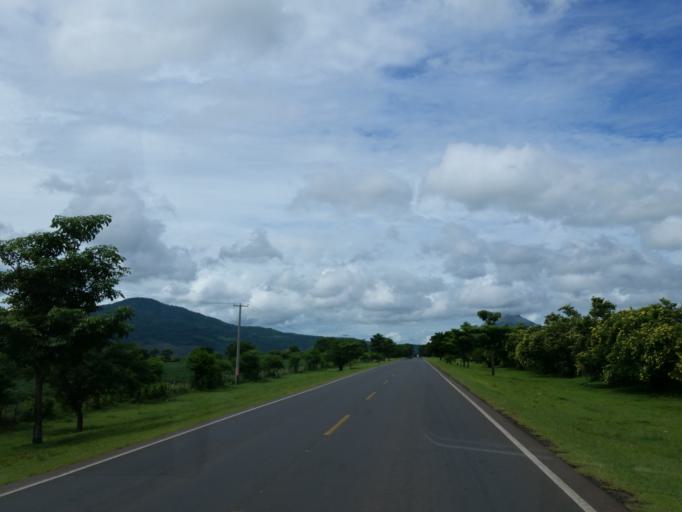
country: NI
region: Leon
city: Larreynaga
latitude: 12.5991
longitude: -86.6949
